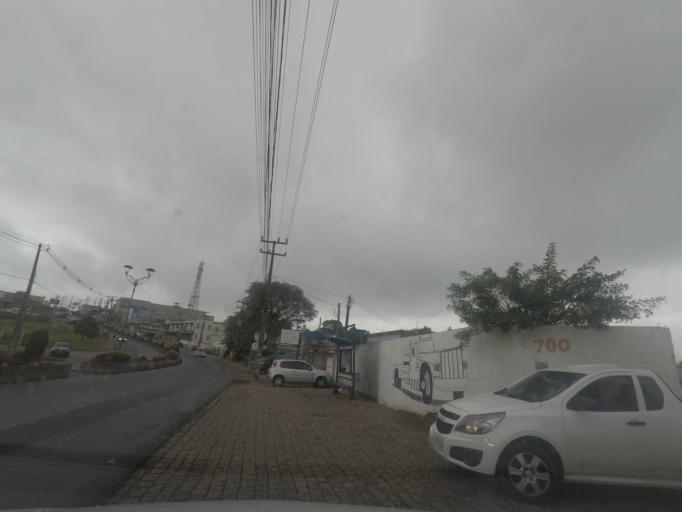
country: BR
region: Parana
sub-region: Quatro Barras
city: Quatro Barras
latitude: -25.3682
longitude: -49.0785
